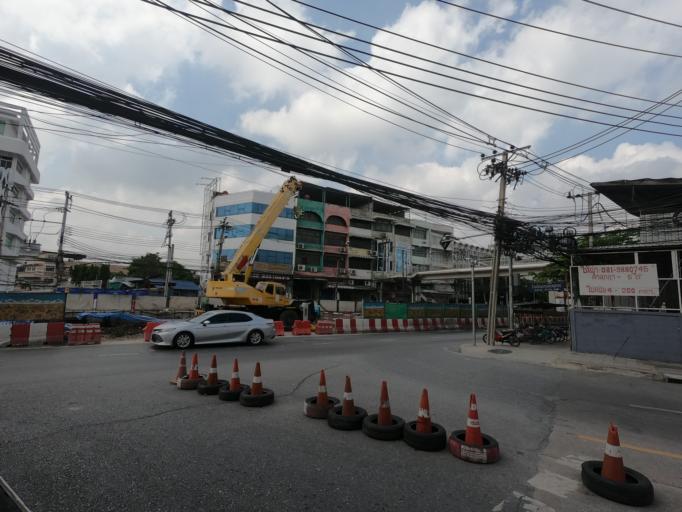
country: TH
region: Bangkok
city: Huai Khwang
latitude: 13.7797
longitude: 100.5861
